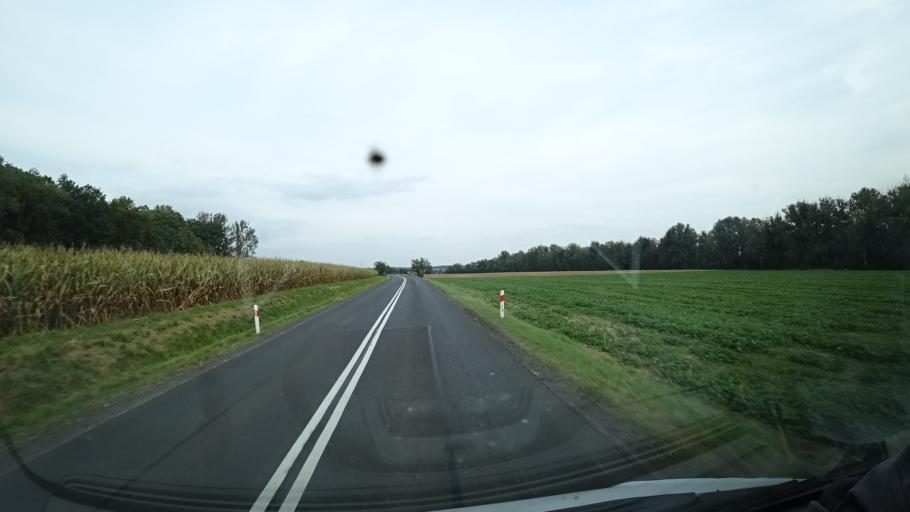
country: PL
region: Silesian Voivodeship
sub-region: Powiat gliwicki
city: Rudziniec
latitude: 50.3966
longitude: 18.4669
